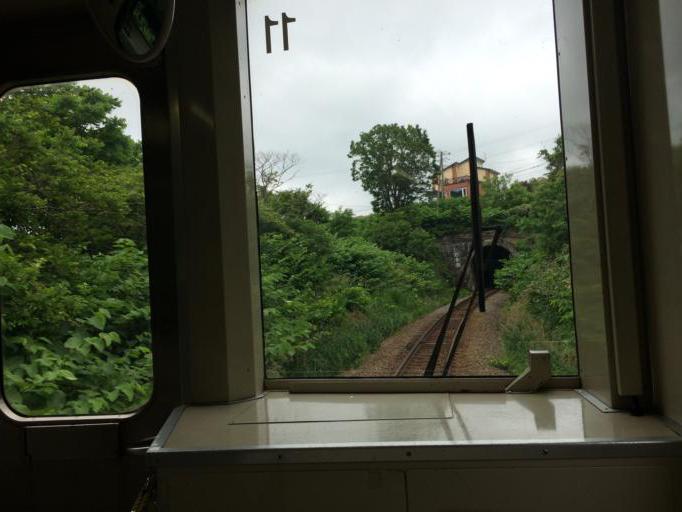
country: JP
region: Hokkaido
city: Otaru
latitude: 43.2190
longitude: 140.9479
